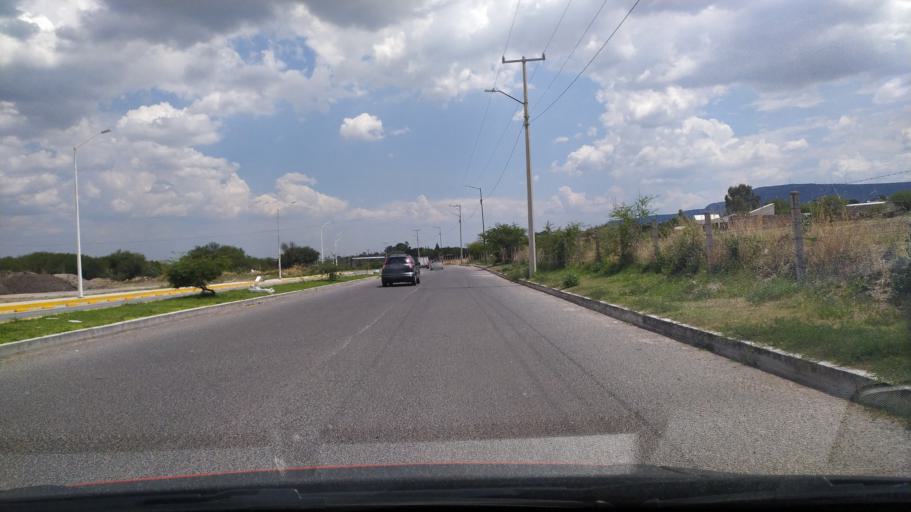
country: MX
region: Guanajuato
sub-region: Purisima del Rincon
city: Potrerillos (Guanajal)
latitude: 21.0526
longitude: -101.8687
